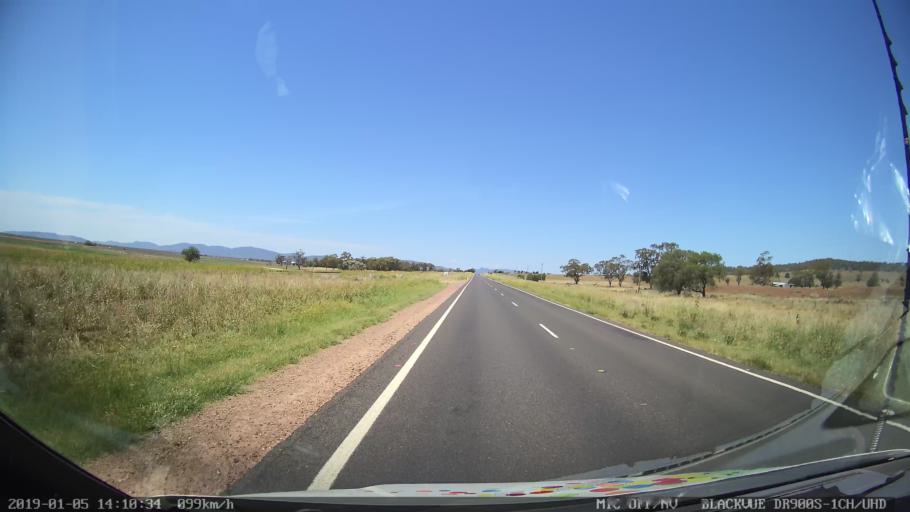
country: AU
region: New South Wales
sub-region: Gunnedah
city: Gunnedah
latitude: -31.2456
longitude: 150.4444
